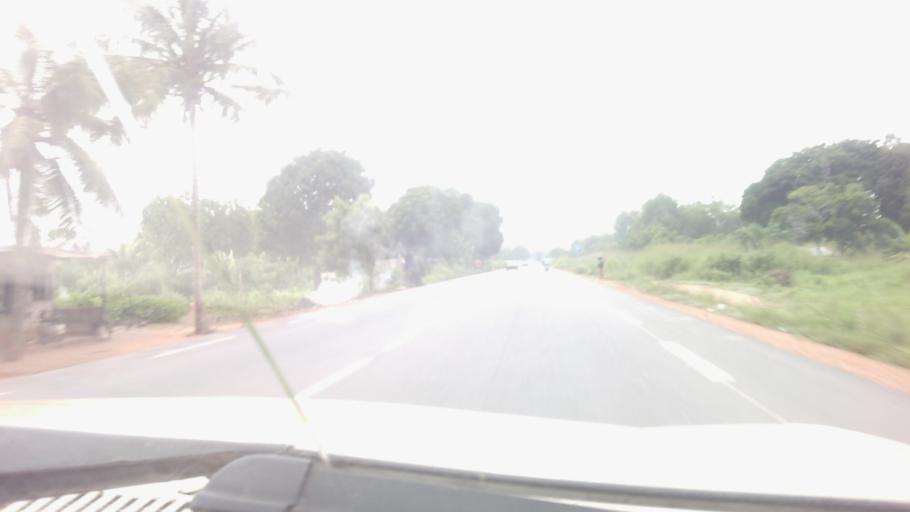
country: BJ
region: Mono
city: Come
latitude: 6.3991
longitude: 1.9578
